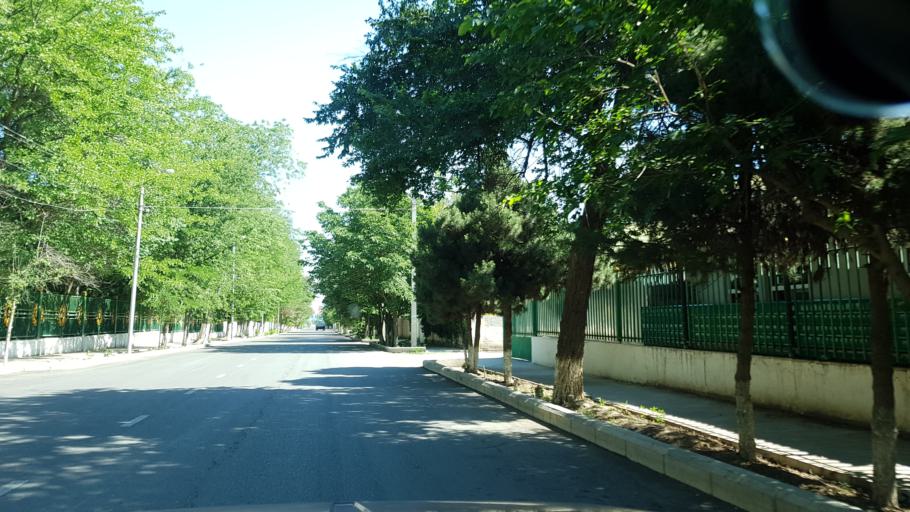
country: TM
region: Ahal
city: Ashgabat
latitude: 37.9534
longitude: 58.3490
